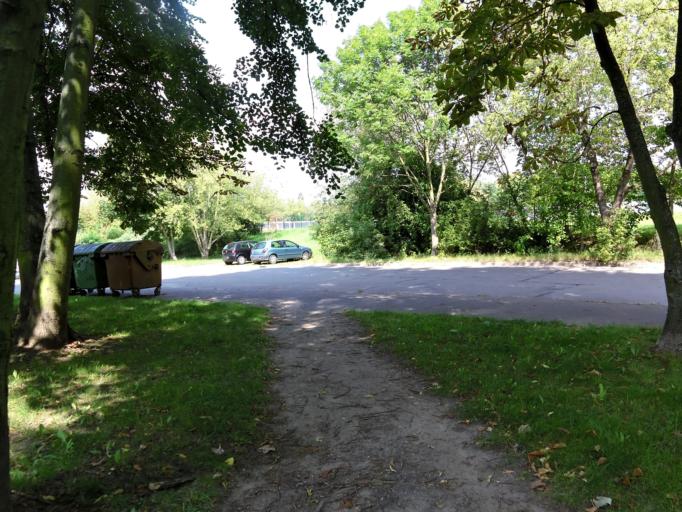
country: DE
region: Saxony
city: Leipzig
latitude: 51.3715
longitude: 12.3452
